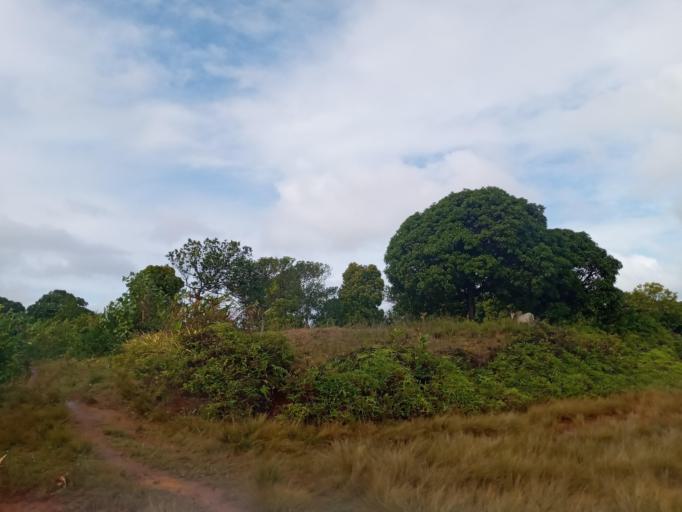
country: MG
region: Atsimo-Atsinanana
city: Vohipaho
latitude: -23.7938
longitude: 47.5506
